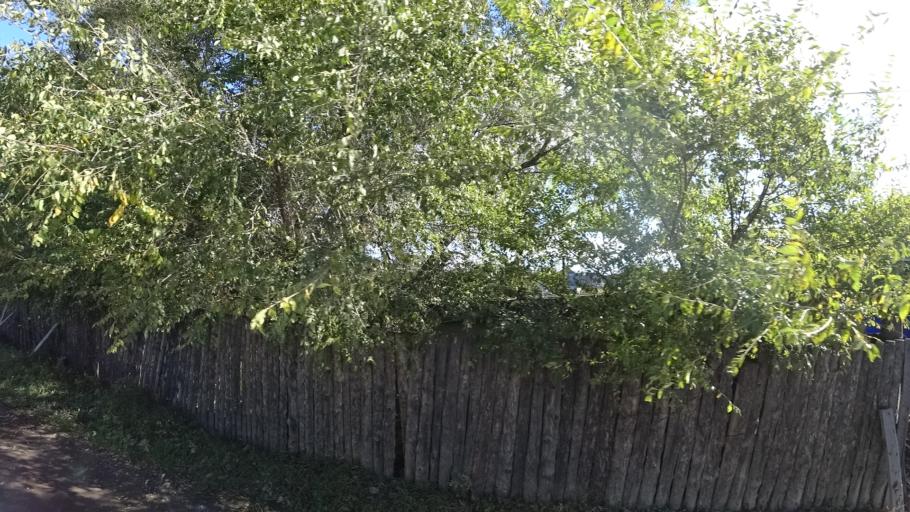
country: RU
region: Khabarovsk Krai
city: Amursk
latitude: 50.2351
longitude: 136.9192
